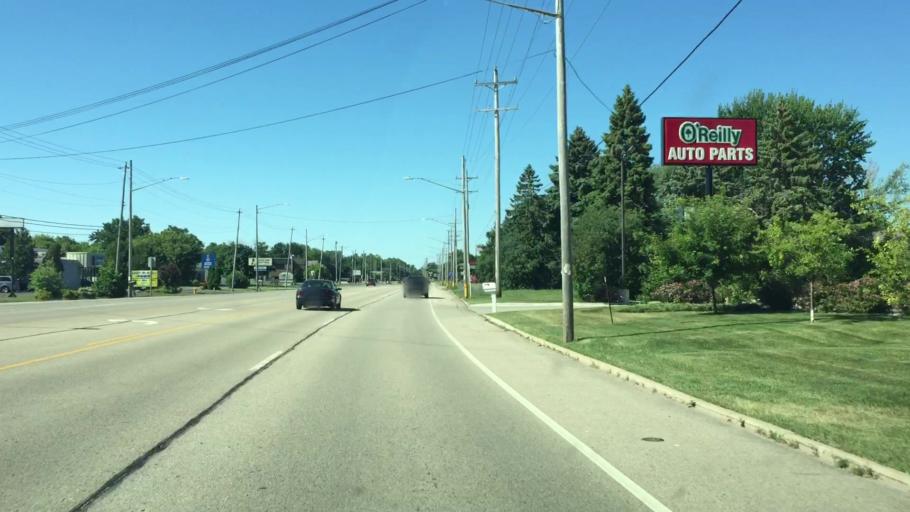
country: US
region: Wisconsin
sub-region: Winnebago County
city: Menasha
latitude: 44.2256
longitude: -88.4249
